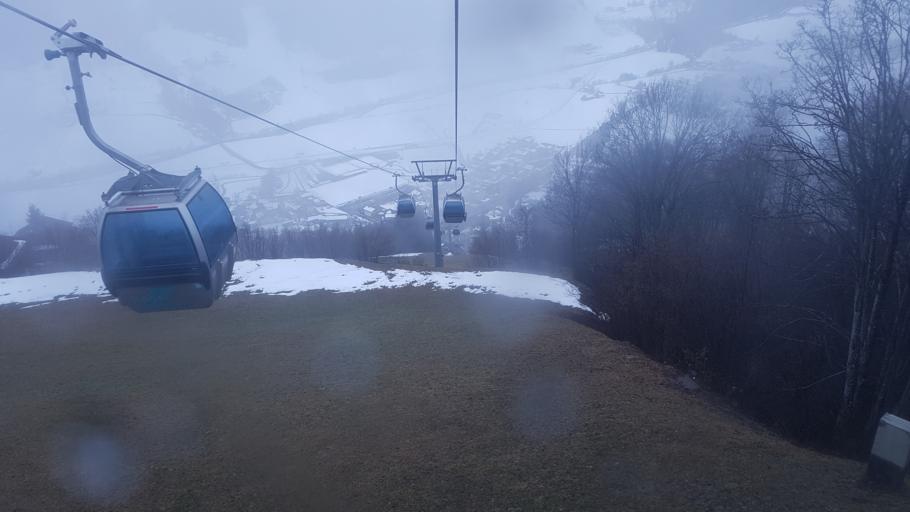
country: AT
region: Salzburg
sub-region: Politischer Bezirk Zell am See
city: Neukirchen am Grossvenediger
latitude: 47.2598
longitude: 12.2809
